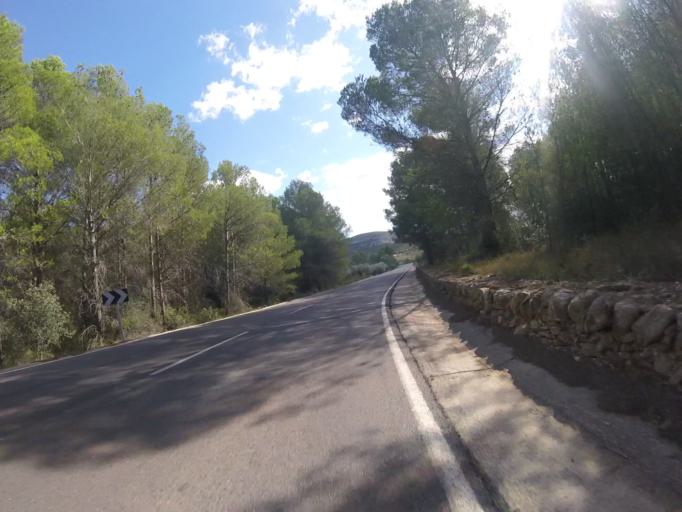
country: ES
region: Valencia
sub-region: Provincia de Castello
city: Cuevas de Vinroma
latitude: 40.3039
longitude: 0.1644
